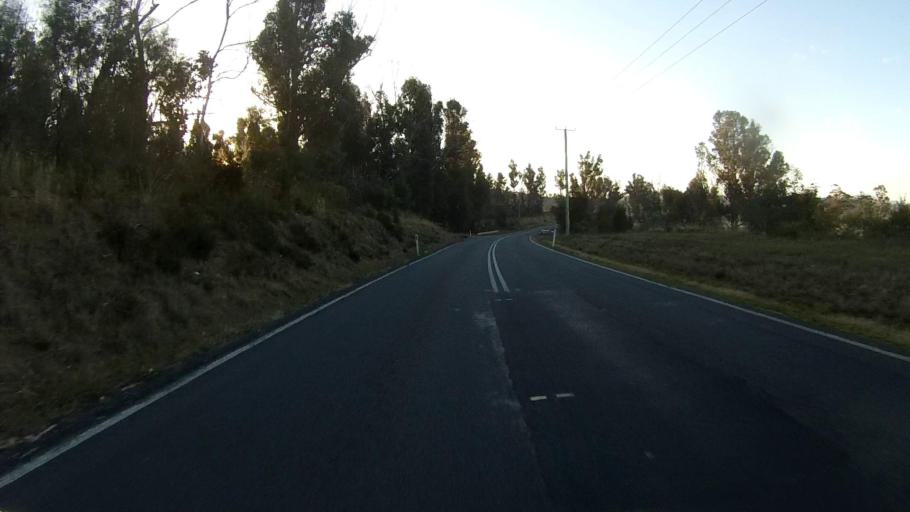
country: AU
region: Tasmania
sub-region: Sorell
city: Sorell
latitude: -42.8711
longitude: 147.8227
